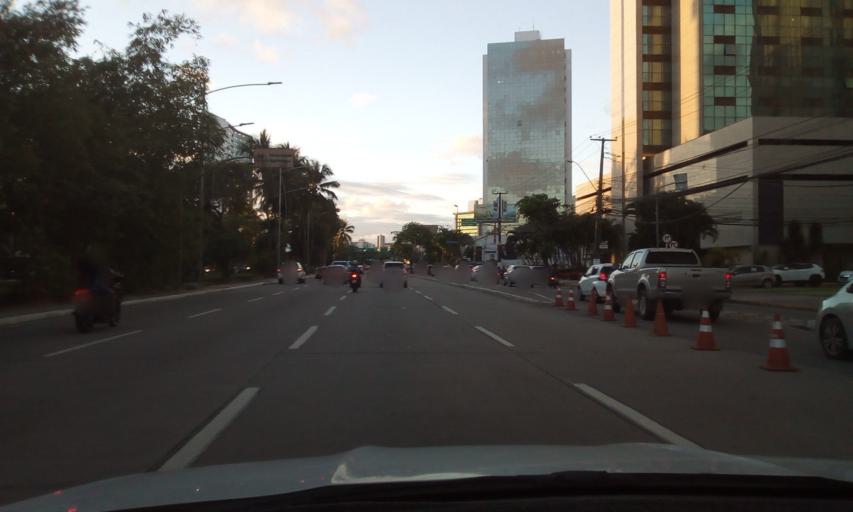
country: BR
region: Pernambuco
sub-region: Recife
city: Recife
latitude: -8.0648
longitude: -34.8971
